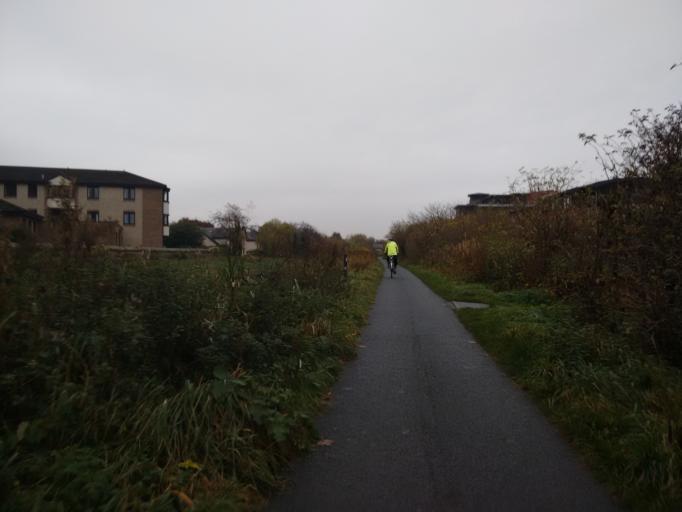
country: GB
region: Scotland
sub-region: Edinburgh
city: Colinton
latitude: 55.9265
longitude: -3.2346
